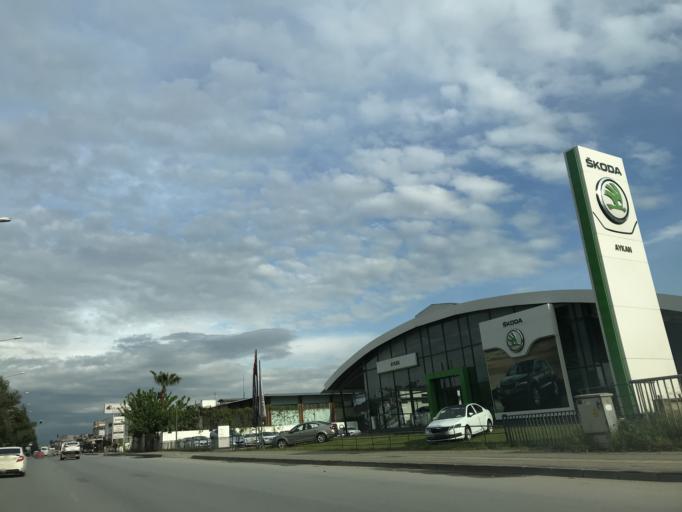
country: TR
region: Adana
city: Seyhan
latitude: 36.9954
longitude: 35.2712
